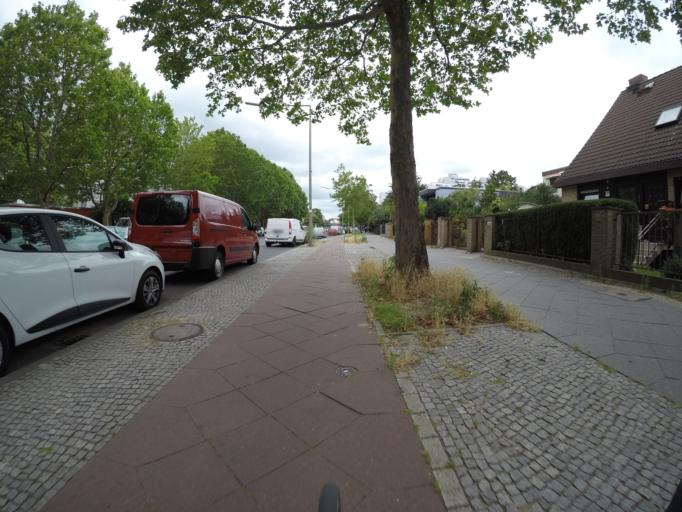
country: DE
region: Berlin
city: Markisches Viertel
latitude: 52.5960
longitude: 13.3415
